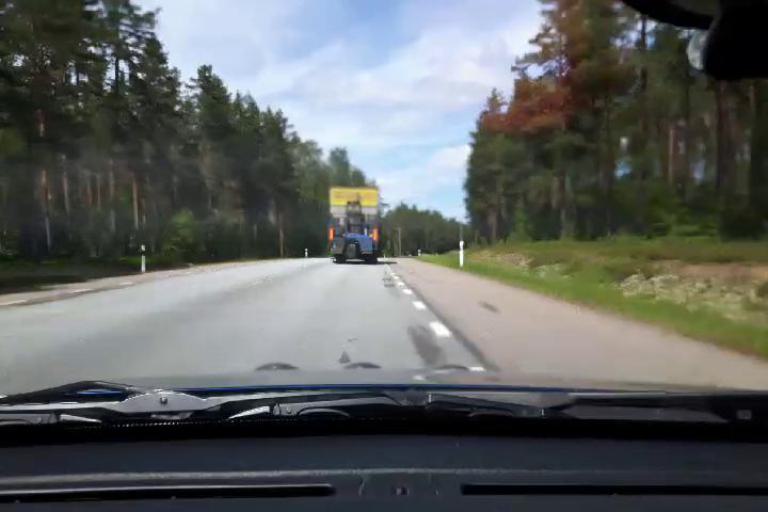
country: SE
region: Uppsala
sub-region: Tierps Kommun
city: Tierp
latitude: 60.1874
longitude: 17.4781
